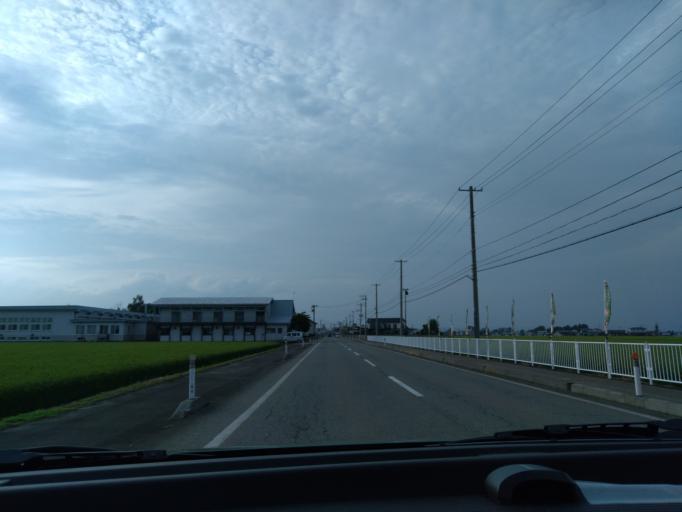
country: JP
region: Akita
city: Omagari
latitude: 39.3997
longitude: 140.5200
